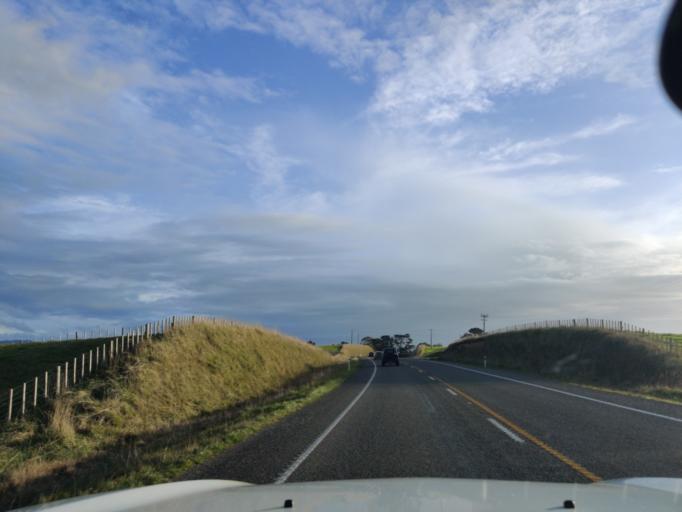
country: NZ
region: Manawatu-Wanganui
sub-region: Horowhenua District
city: Foxton
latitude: -40.5110
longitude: 175.4683
